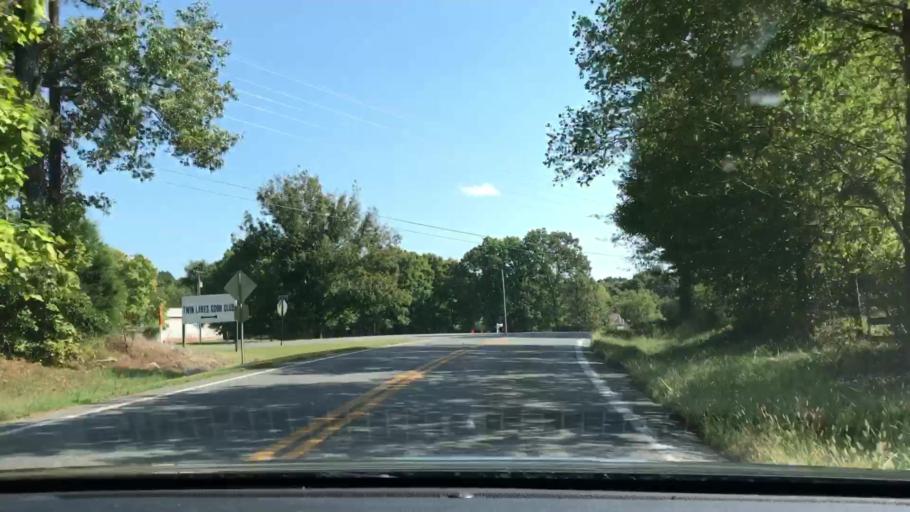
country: US
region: Kentucky
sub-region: Marshall County
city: Benton
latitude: 36.7658
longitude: -88.2675
